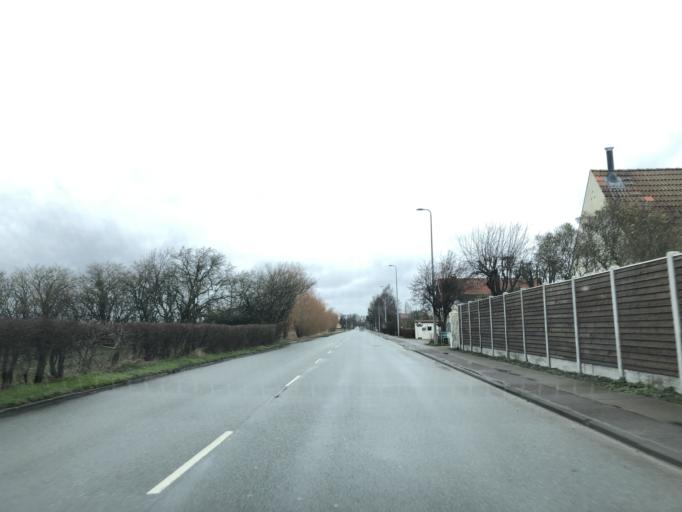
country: DK
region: Capital Region
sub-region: Dragor Kommune
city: Dragor
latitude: 55.5860
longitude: 12.6359
